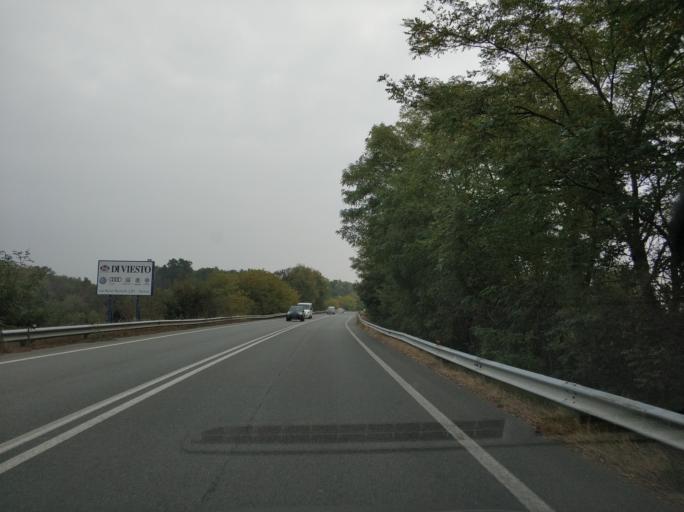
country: IT
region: Piedmont
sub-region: Provincia di Torino
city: Leini
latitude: 45.2078
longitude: 7.7135
